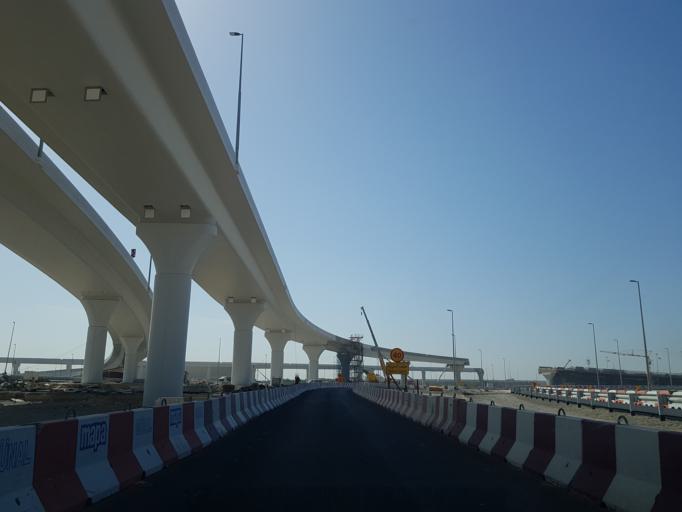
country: AE
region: Dubai
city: Dubai
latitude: 25.0169
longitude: 55.0940
